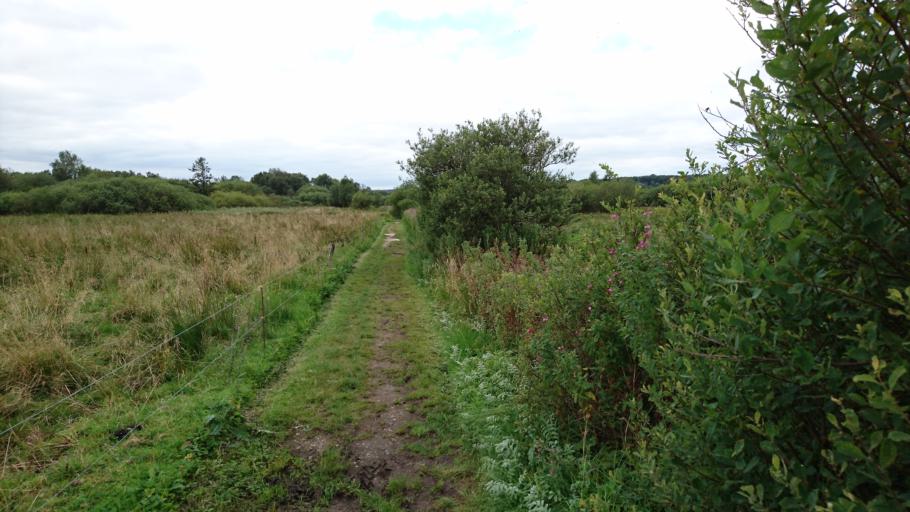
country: DK
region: North Denmark
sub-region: Rebild Kommune
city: Skorping
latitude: 56.7844
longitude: 9.9172
